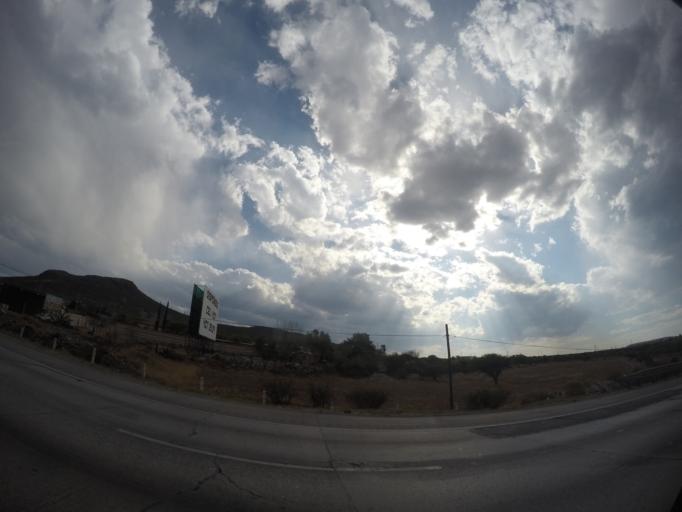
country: MX
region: Mexico
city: San Francisco Soyaniquilpan
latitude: 19.9959
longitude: -99.4818
